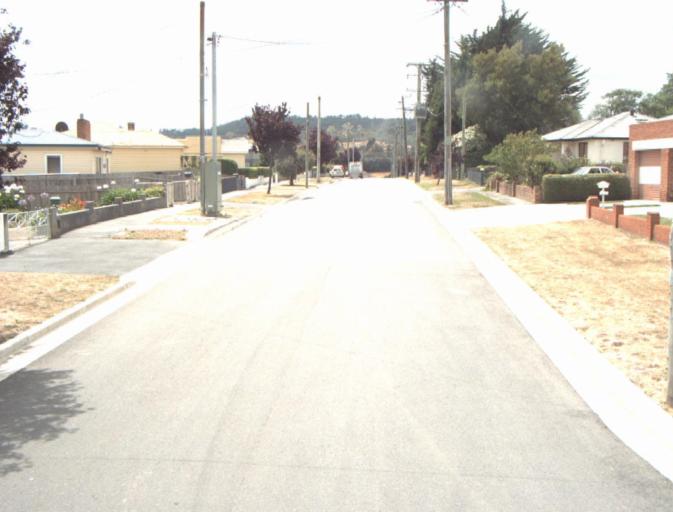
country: AU
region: Tasmania
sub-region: Launceston
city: Newnham
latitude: -41.4113
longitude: 147.1489
